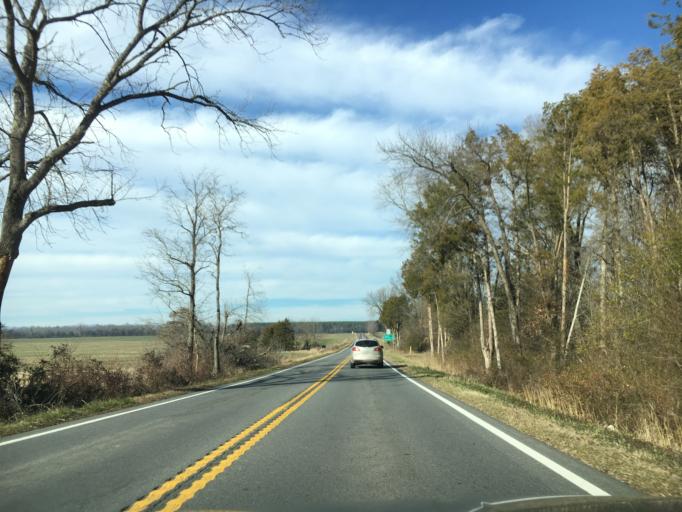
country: US
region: Virginia
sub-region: Culpeper County
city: Culpeper
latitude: 38.3967
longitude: -78.0051
